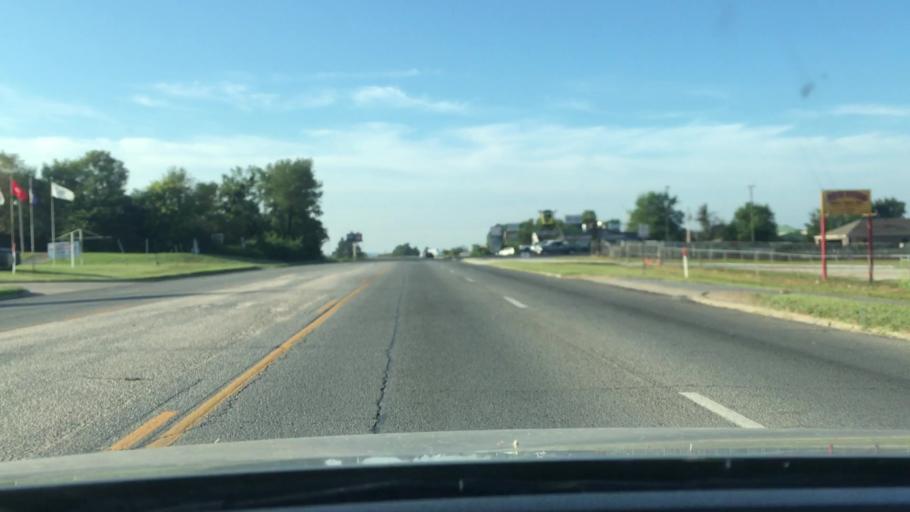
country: US
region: Oklahoma
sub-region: Cherokee County
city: Park Hill
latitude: 35.8681
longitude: -94.9763
